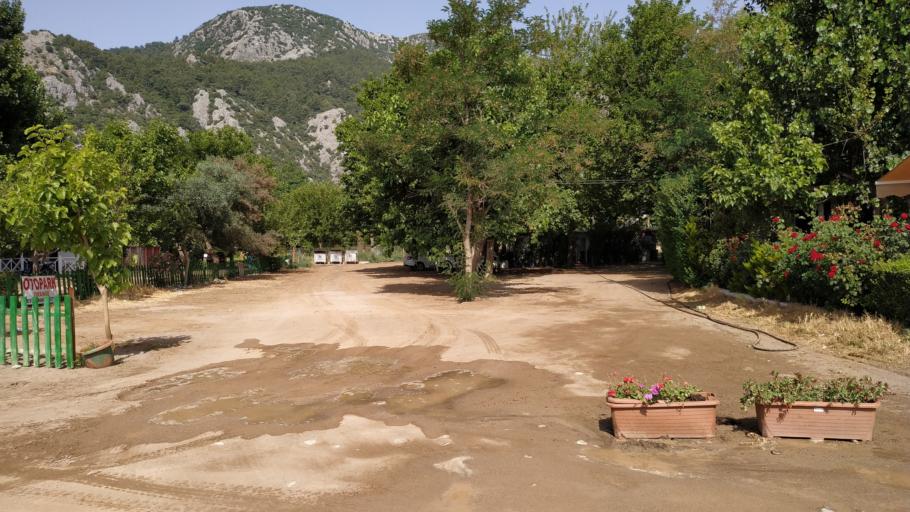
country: TR
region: Antalya
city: Tekirova
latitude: 36.4044
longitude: 30.4778
